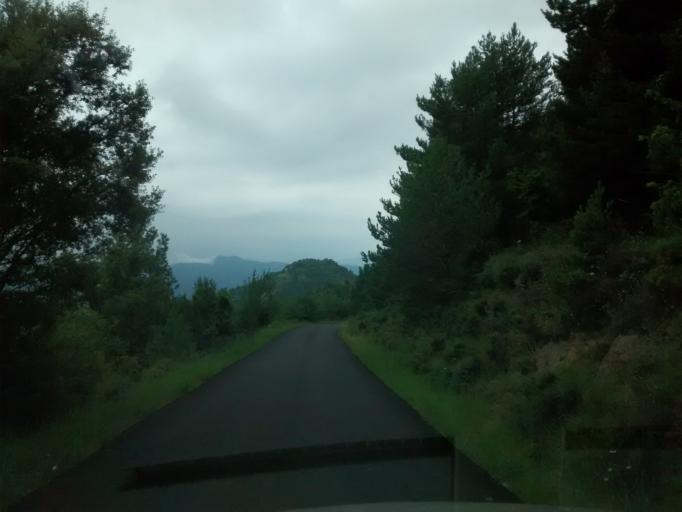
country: ES
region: Aragon
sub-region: Provincia de Huesca
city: Puertolas
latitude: 42.5583
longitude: 0.1409
